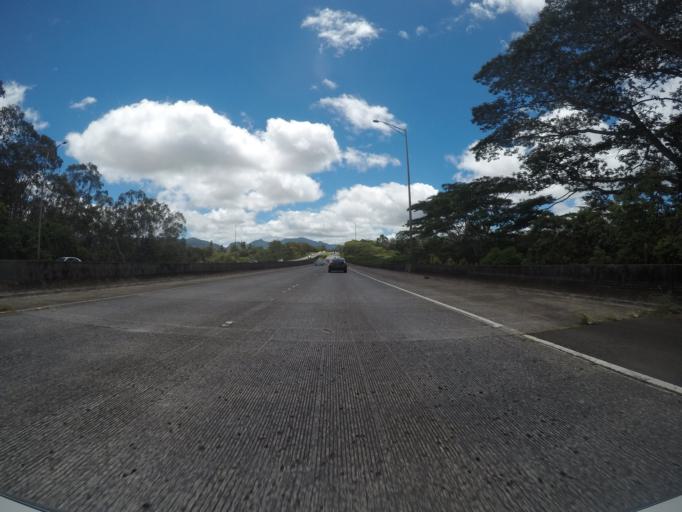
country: US
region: Hawaii
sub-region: Honolulu County
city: Waipi'o Acres
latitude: 21.4744
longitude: -158.0151
